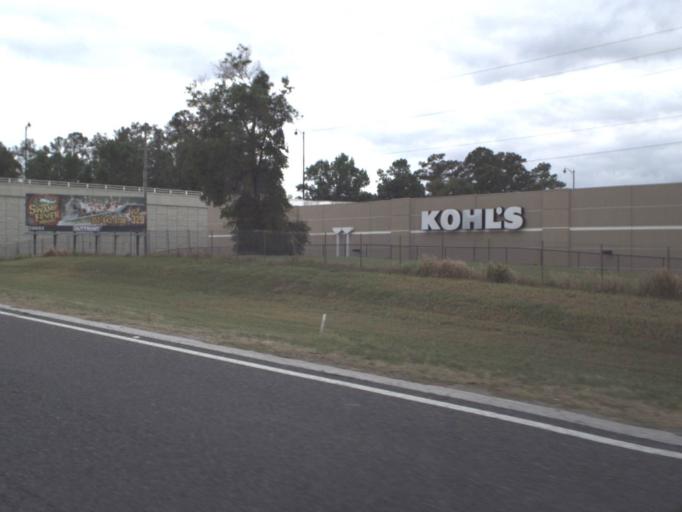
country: US
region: Florida
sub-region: Marion County
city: Ocala
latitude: 29.1438
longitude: -82.1852
